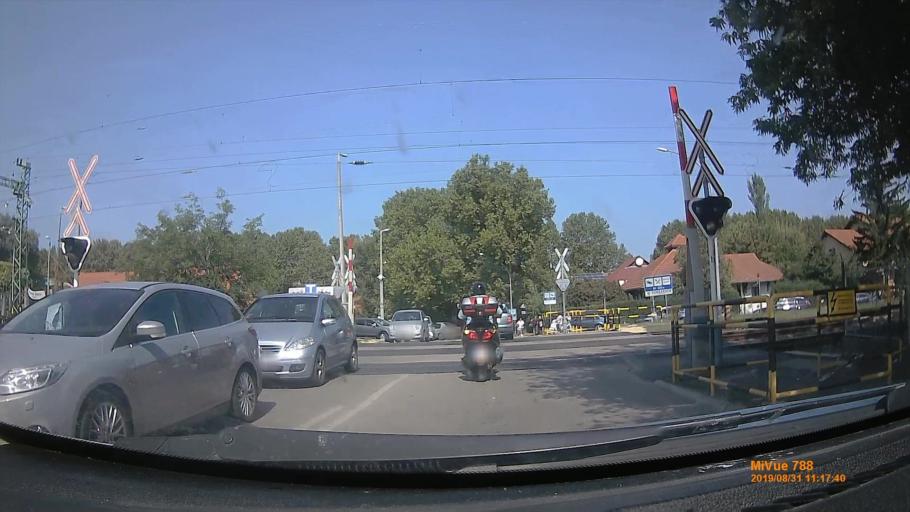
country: HU
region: Somogy
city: Siofok
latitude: 46.9088
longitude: 18.0573
